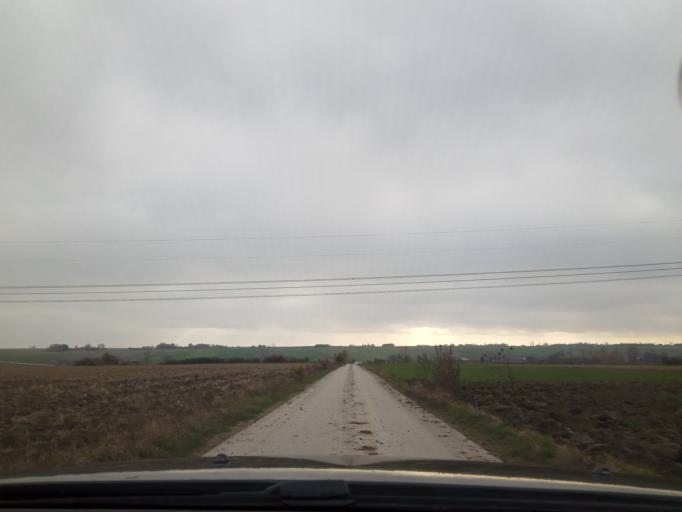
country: PL
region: Swietokrzyskie
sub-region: Powiat jedrzejowski
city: Imielno
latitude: 50.6154
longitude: 20.3928
